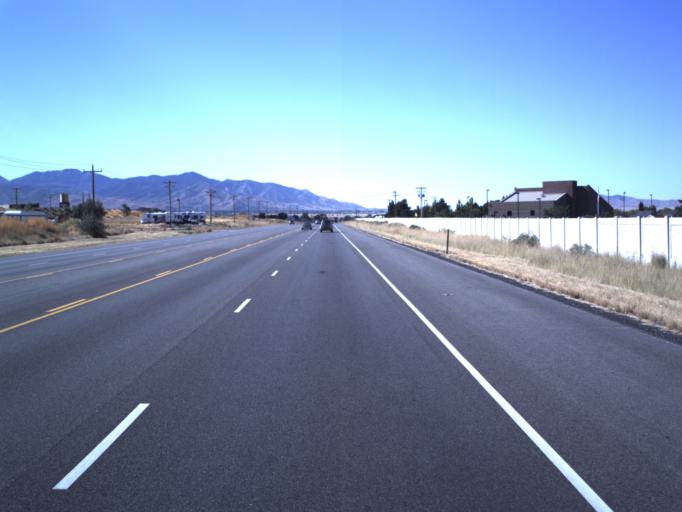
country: US
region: Utah
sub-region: Tooele County
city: Stansbury park
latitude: 40.6383
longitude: -112.2888
